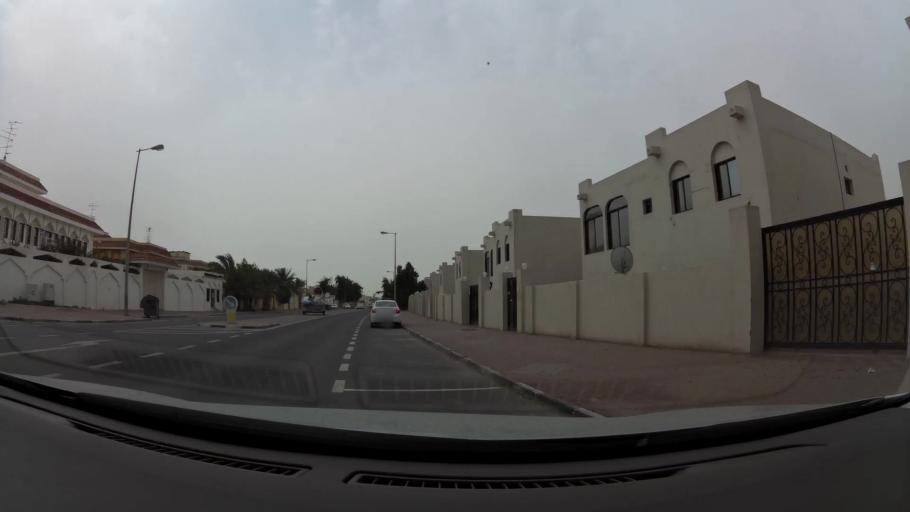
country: QA
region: Baladiyat ad Dawhah
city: Doha
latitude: 25.2522
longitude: 51.5437
